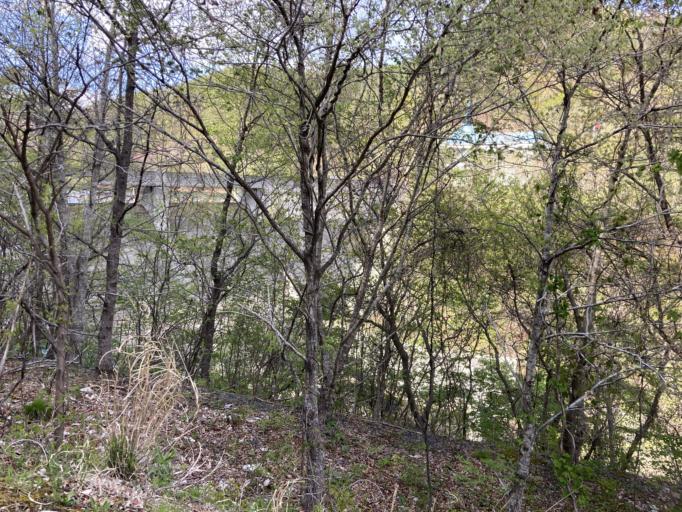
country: JP
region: Iwate
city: Ichinoseki
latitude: 38.8003
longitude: 141.4134
